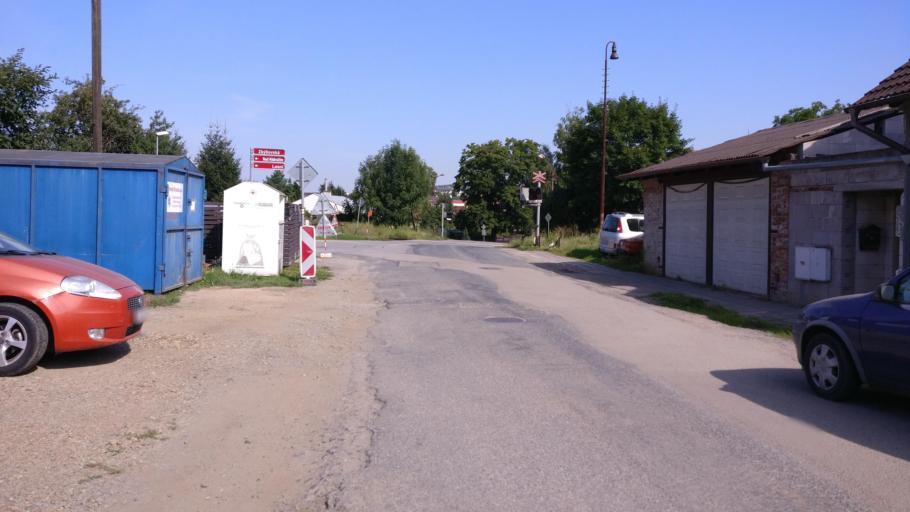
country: CZ
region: South Moravian
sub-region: Okres Brno-Venkov
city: Rosice
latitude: 49.1772
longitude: 16.3873
